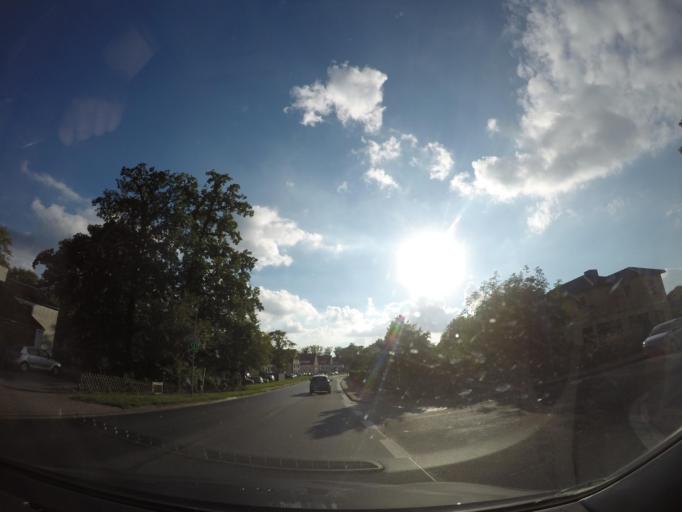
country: DE
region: Lower Saxony
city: Grasleben
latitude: 52.2919
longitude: 11.0004
